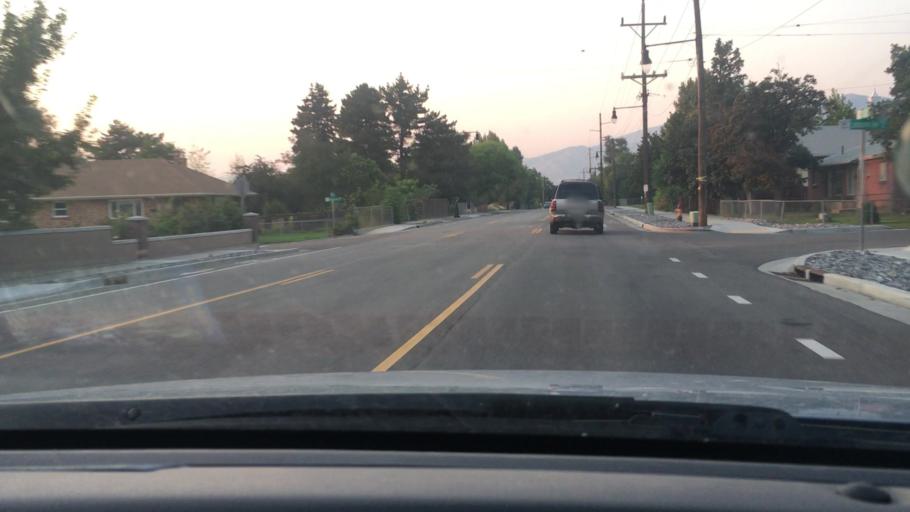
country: US
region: Utah
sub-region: Salt Lake County
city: Canyon Rim
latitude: 40.7023
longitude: -111.8244
